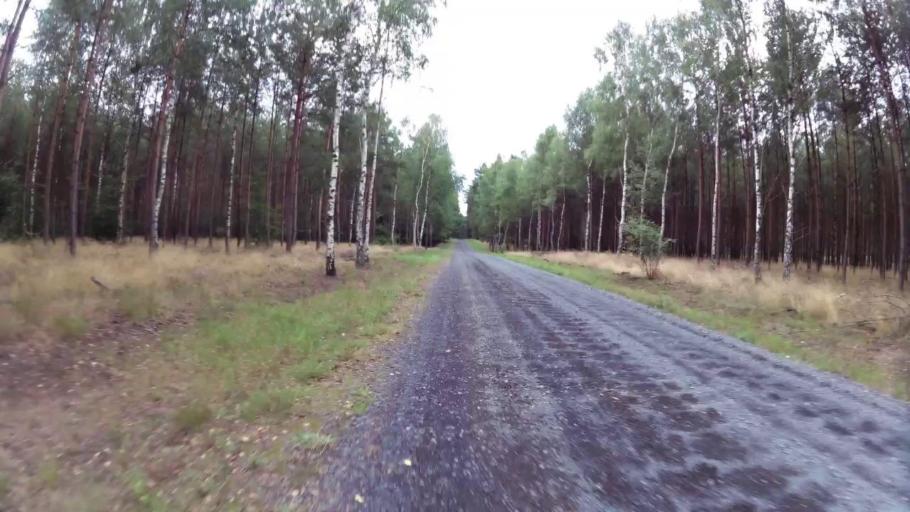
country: PL
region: West Pomeranian Voivodeship
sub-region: Powiat mysliborski
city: Debno
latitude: 52.7905
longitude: 14.7163
